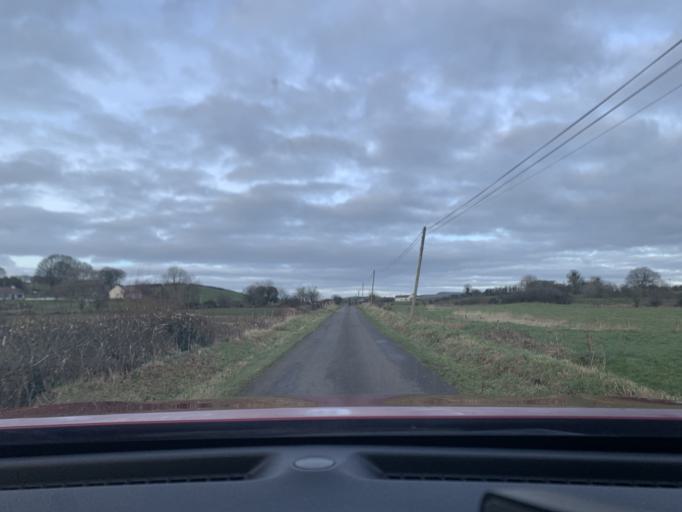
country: IE
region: Connaught
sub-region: Sligo
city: Ballymote
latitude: 54.0493
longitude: -8.5713
